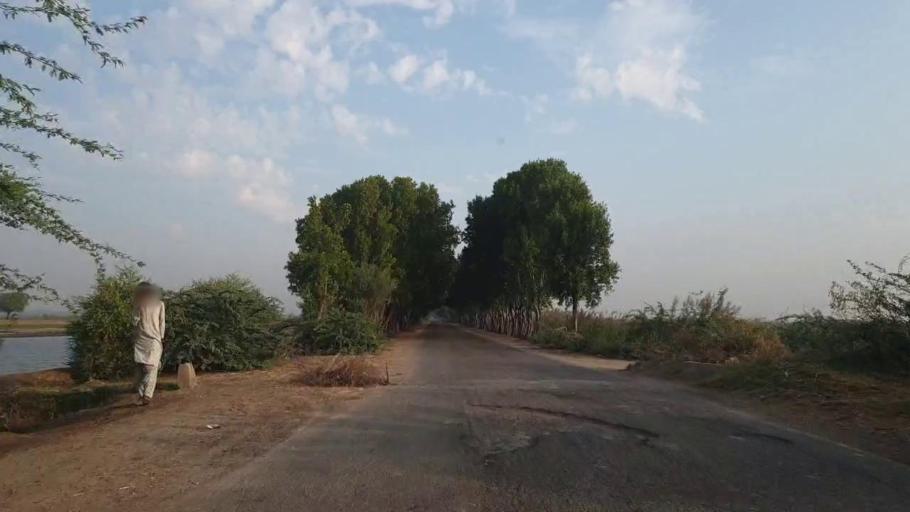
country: PK
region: Sindh
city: Tando Bago
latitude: 24.7267
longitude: 68.9429
